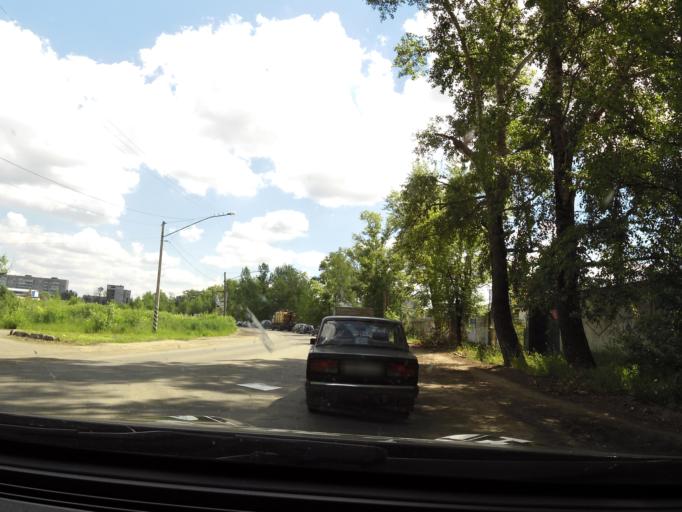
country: RU
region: Vologda
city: Vologda
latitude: 59.2289
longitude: 39.8538
